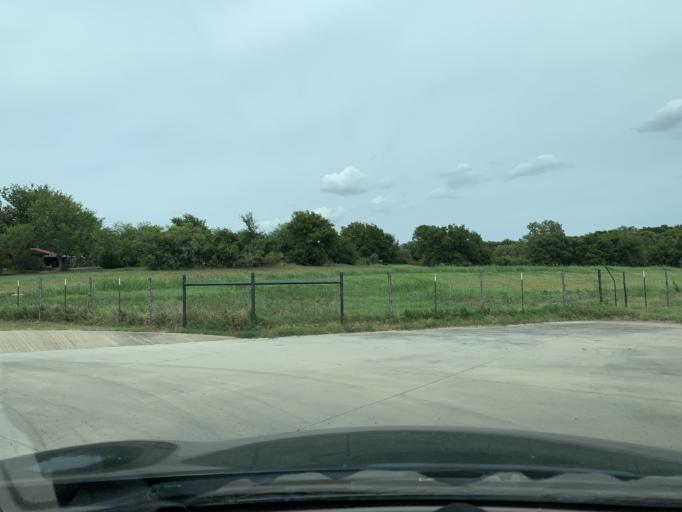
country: US
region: Texas
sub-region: Dallas County
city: Grand Prairie
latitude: 32.6662
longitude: -97.0302
